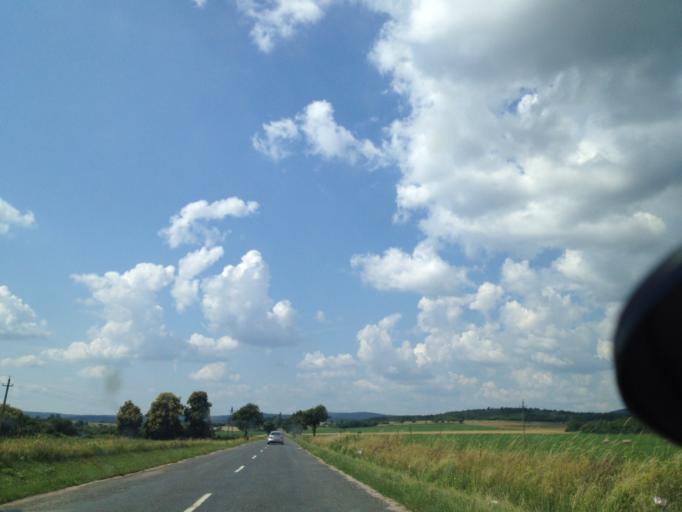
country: HU
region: Veszprem
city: Urkut
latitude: 46.9994
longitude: 17.7305
